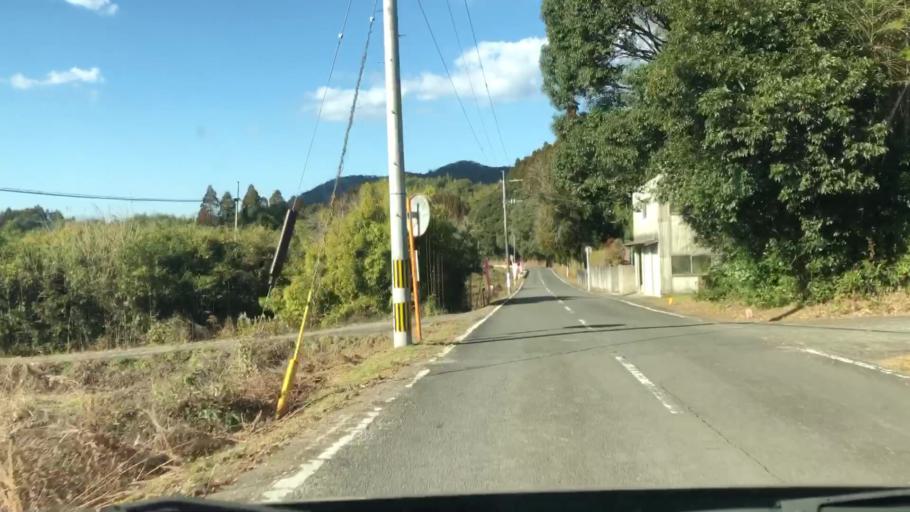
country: JP
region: Kagoshima
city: Satsumasendai
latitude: 31.8557
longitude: 130.3608
